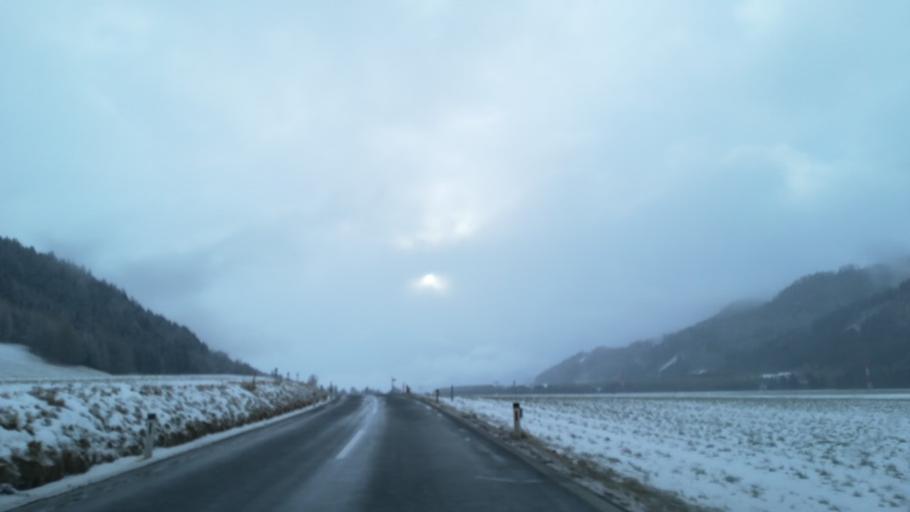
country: AT
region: Styria
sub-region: Politischer Bezirk Murtal
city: Poels
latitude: 47.2161
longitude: 14.6155
